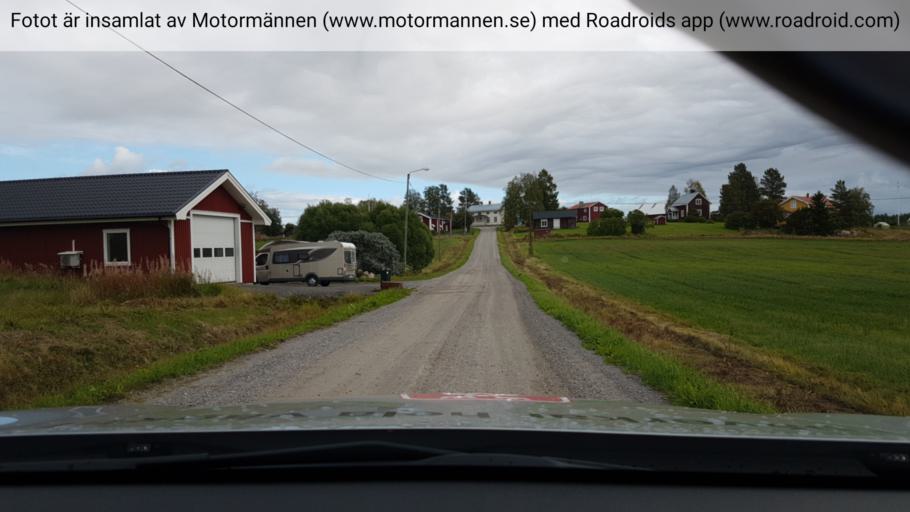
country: SE
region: Vaesterbotten
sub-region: Skelleftea Kommun
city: Byske
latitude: 65.1173
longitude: 21.2054
